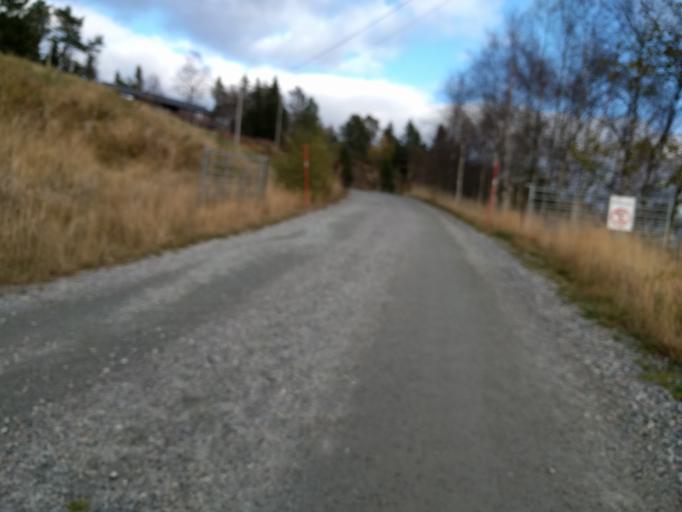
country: NO
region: Aust-Agder
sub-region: Evje og Hornnes
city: Evje
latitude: 58.6510
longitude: 7.9518
